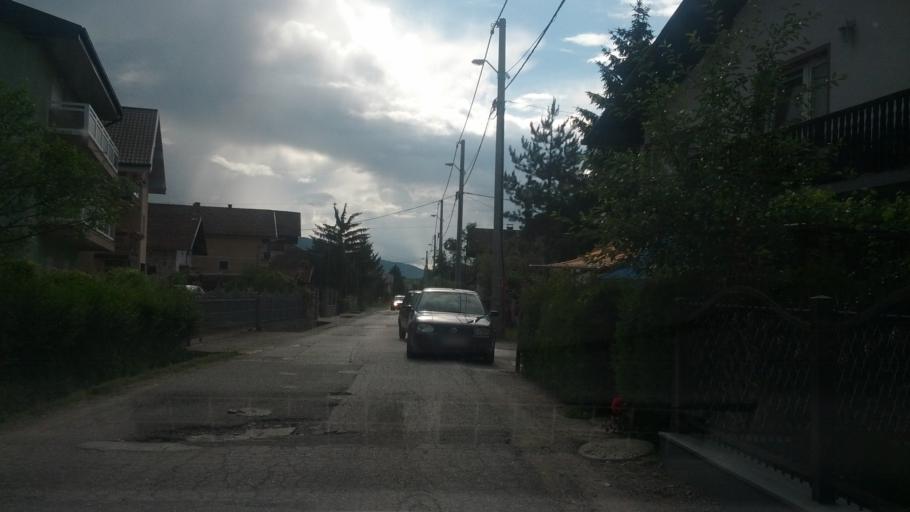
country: BA
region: Federation of Bosnia and Herzegovina
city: Bihac
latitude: 44.8409
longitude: 15.8800
